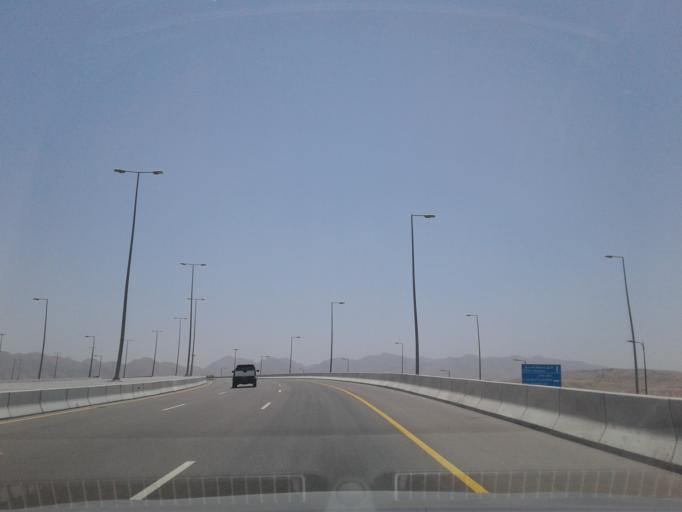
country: OM
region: Muhafazat Masqat
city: Bawshar
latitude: 23.5728
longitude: 58.3327
